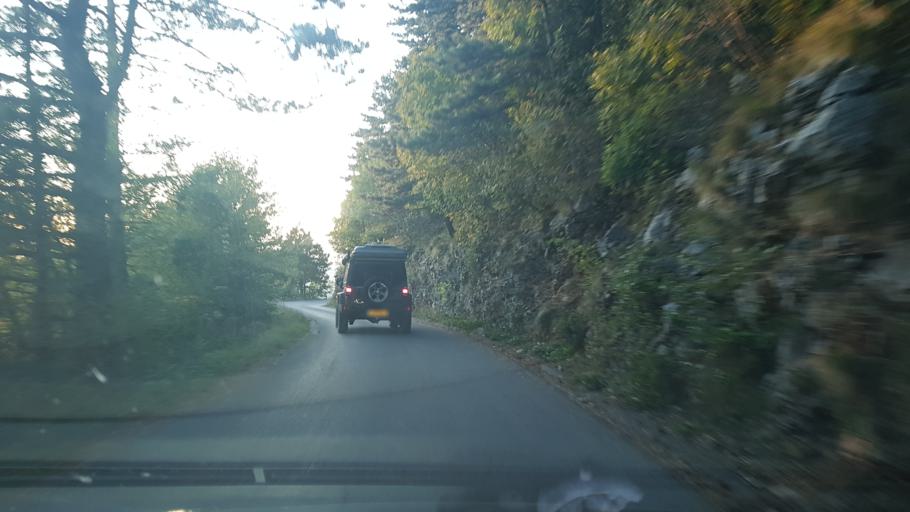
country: SI
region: Vipava
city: Vipava
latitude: 45.7985
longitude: 14.0054
